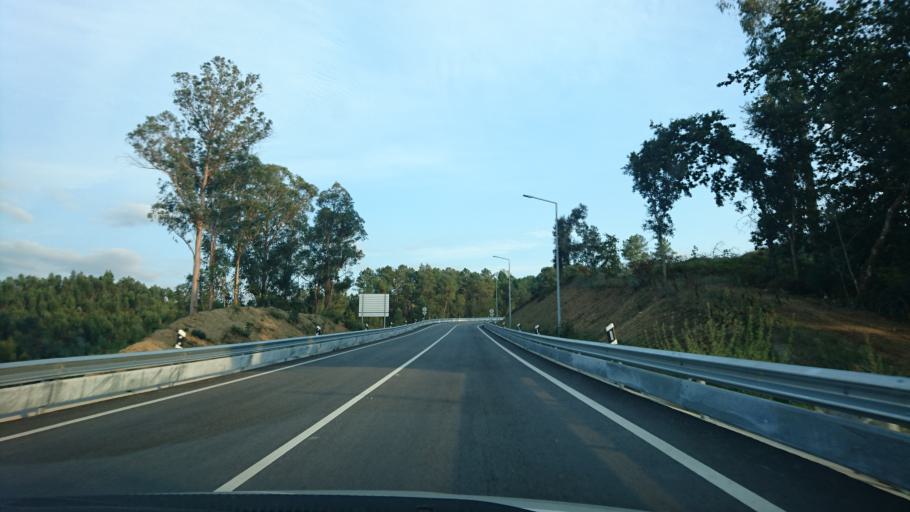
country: PT
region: Braga
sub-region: Celorico de Basto
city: Celorico de Basto
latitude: 41.4079
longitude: -7.9828
